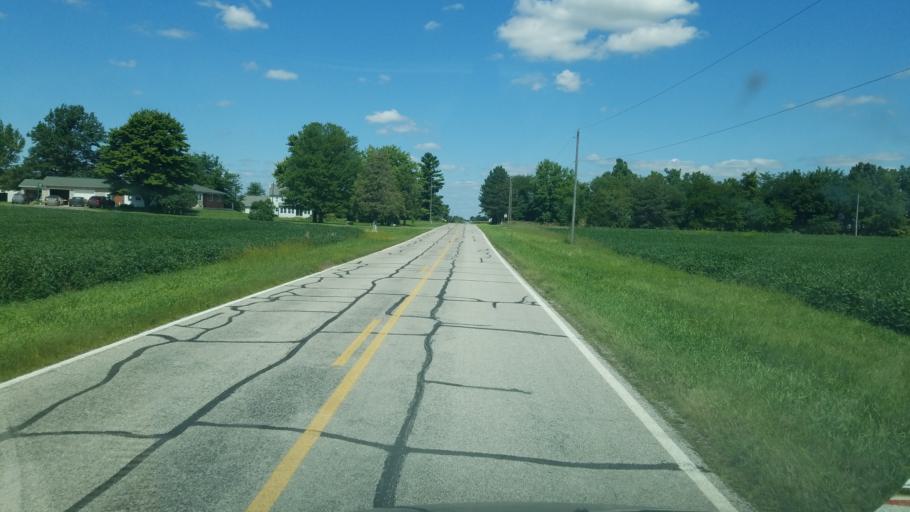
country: US
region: Ohio
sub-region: Fulton County
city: Delta
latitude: 41.6479
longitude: -84.0157
